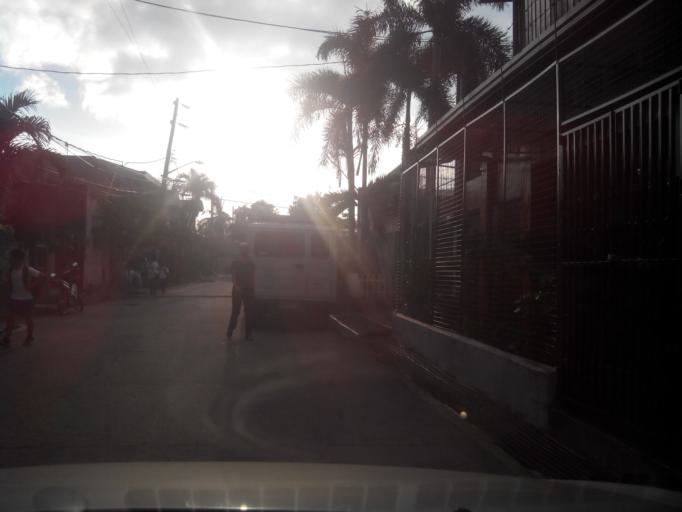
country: PH
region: Calabarzon
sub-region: Province of Rizal
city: Taytay
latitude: 14.5651
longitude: 121.1274
